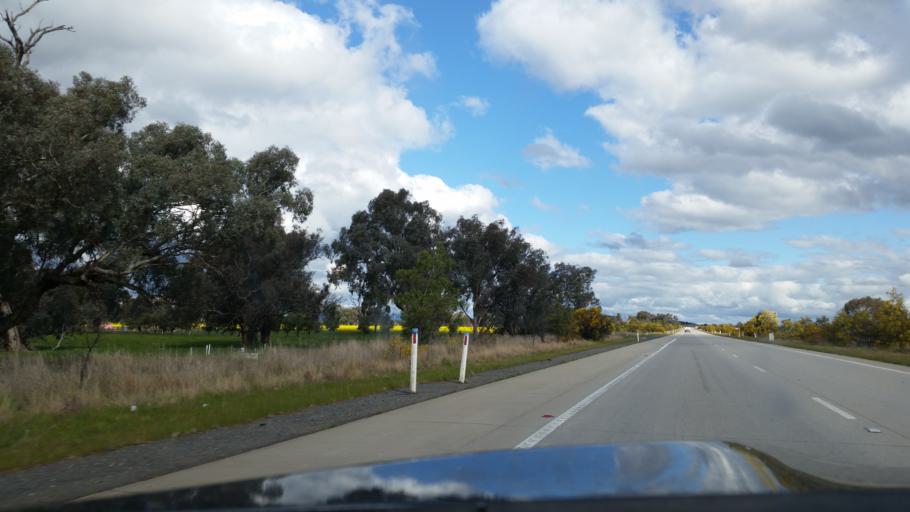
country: AU
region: New South Wales
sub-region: Greater Hume Shire
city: Jindera
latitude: -35.9445
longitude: 147.0037
